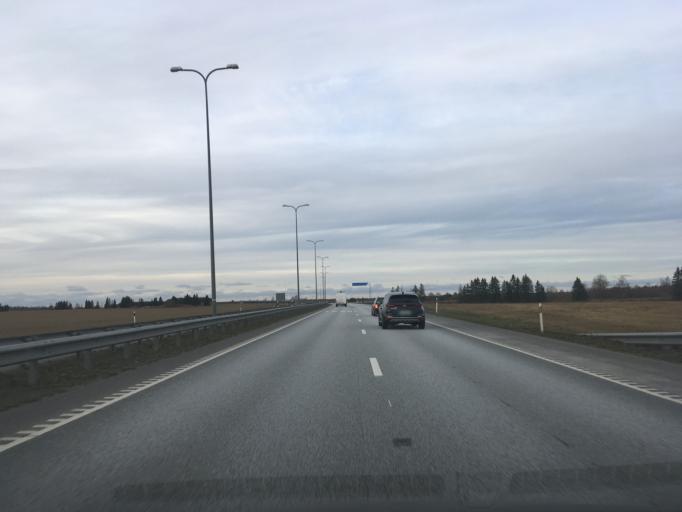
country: EE
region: Ida-Virumaa
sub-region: Kohtla-Jaerve linn
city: Kohtla-Jarve
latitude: 59.3965
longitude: 27.3344
